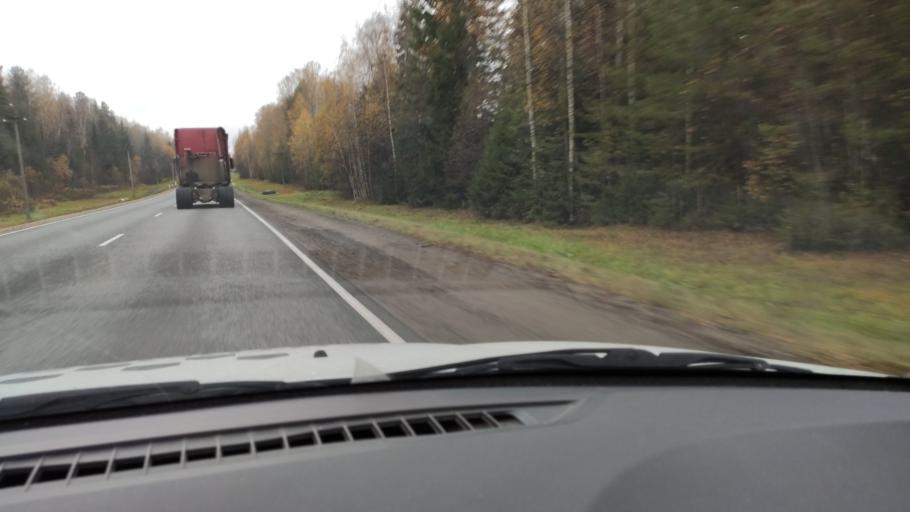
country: RU
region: Kirov
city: Belaya Kholunitsa
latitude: 58.8484
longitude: 50.7174
